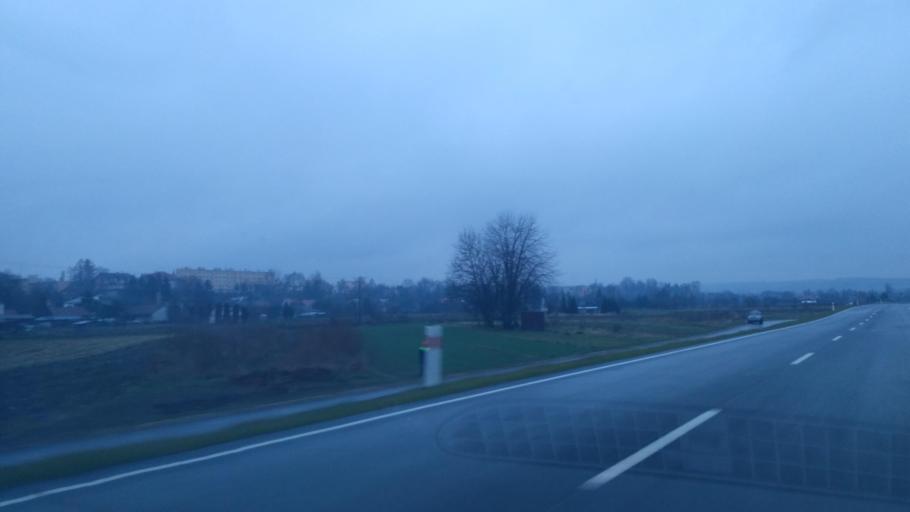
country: PL
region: Subcarpathian Voivodeship
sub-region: Powiat rzeszowski
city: Dynow
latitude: 49.8104
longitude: 22.2406
